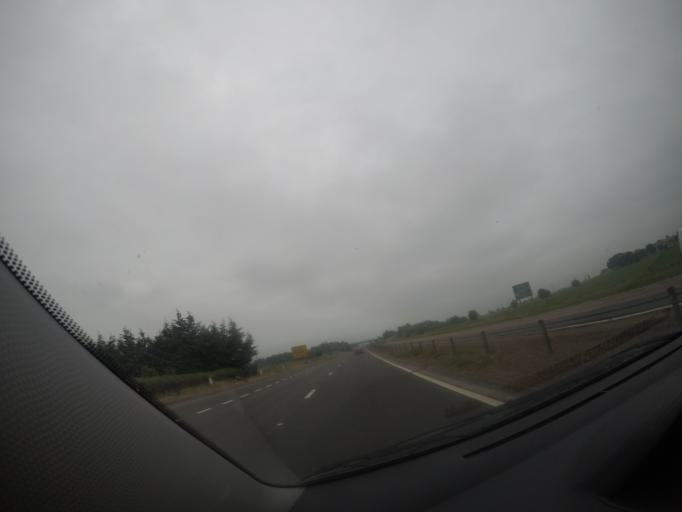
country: GB
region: Scotland
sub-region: Perth and Kinross
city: Errol
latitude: 56.4165
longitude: -3.2356
